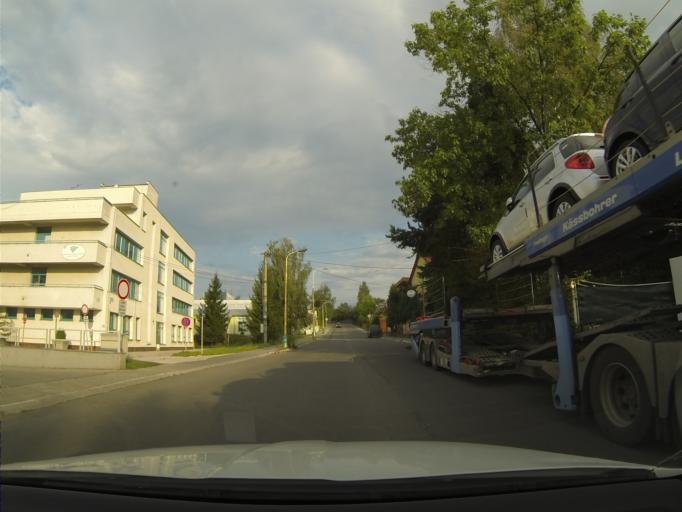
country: SK
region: Nitriansky
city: Prievidza
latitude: 48.7782
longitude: 18.6269
